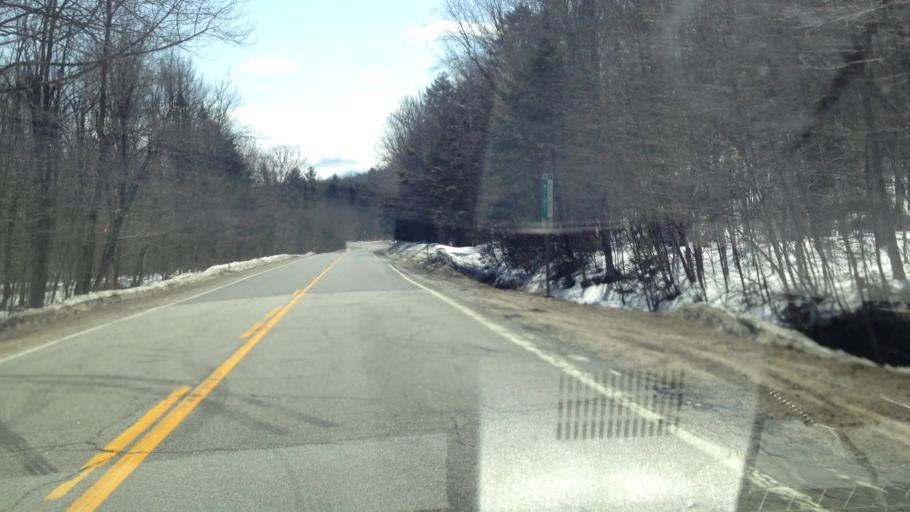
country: US
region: New Hampshire
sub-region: Sullivan County
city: Springfield
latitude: 43.4832
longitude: -71.9758
